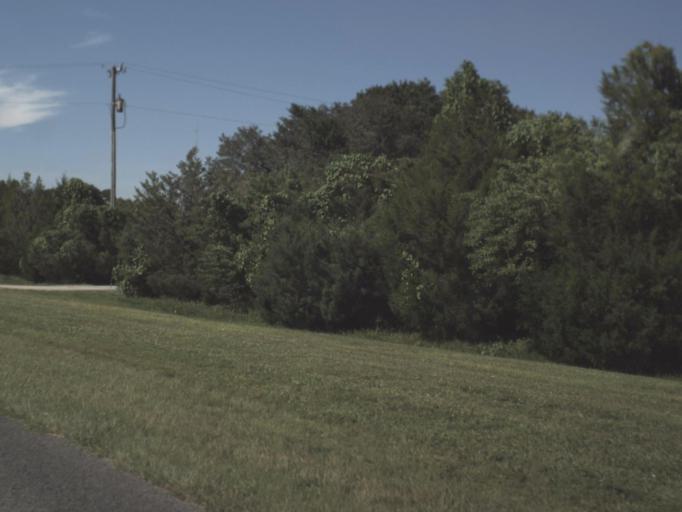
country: US
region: Florida
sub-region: Hendry County
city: Clewiston
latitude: 26.7544
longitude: -80.9131
